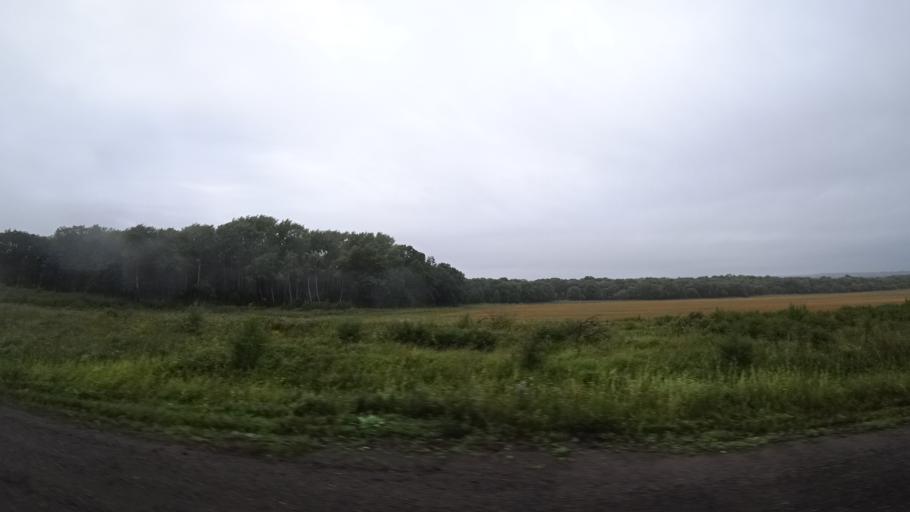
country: RU
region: Primorskiy
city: Monastyrishche
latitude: 44.2780
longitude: 132.4884
